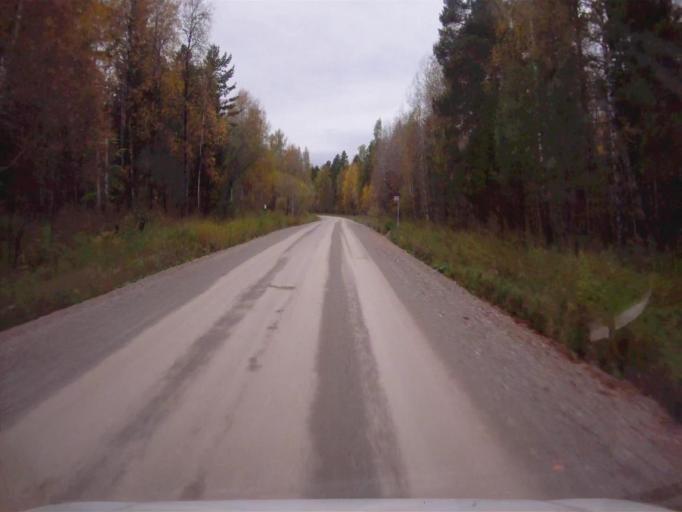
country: RU
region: Chelyabinsk
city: Nyazepetrovsk
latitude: 56.0651
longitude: 59.4406
